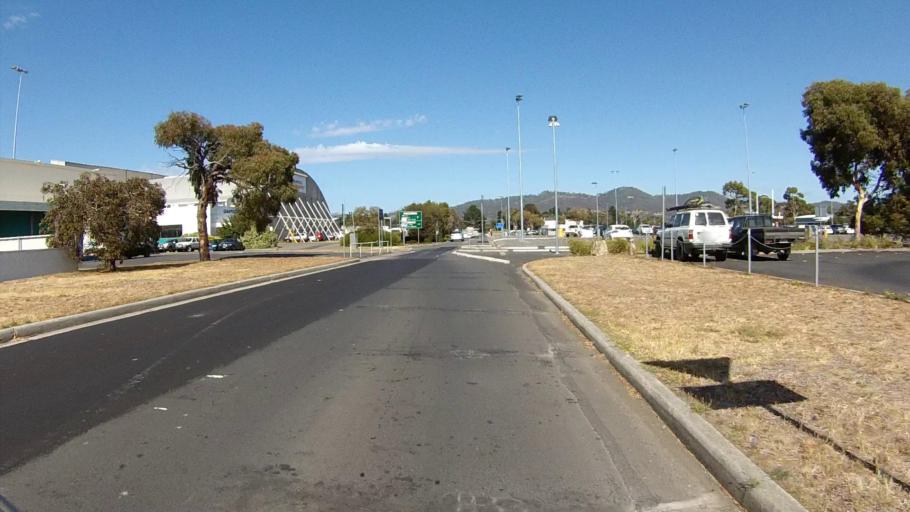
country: AU
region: Tasmania
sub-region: Clarence
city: Seven Mile Beach
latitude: -42.8386
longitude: 147.5066
